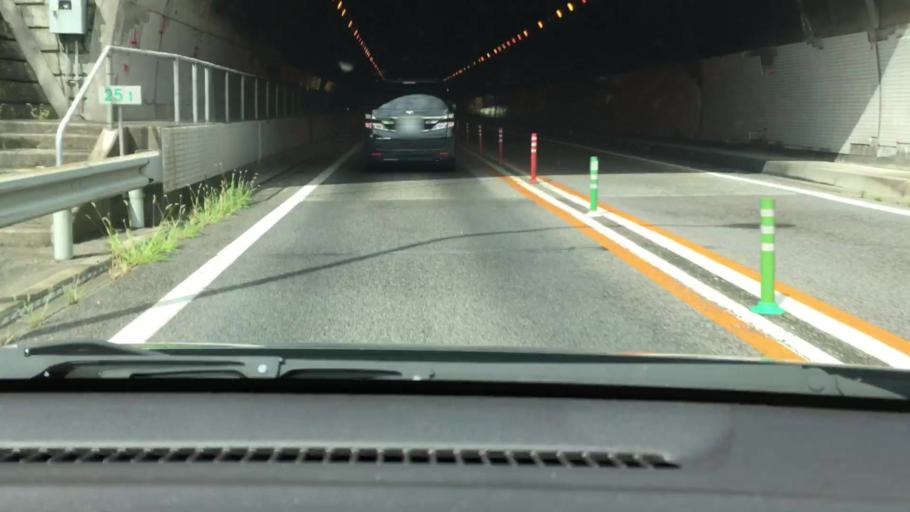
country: JP
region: Nagasaki
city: Sasebo
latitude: 33.1506
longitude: 129.7437
